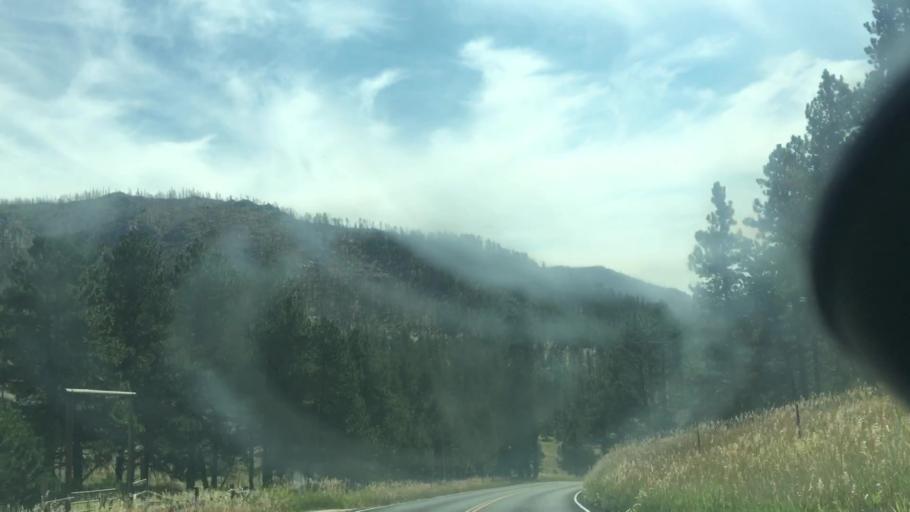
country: US
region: Colorado
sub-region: Larimer County
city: Laporte
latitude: 40.6031
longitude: -105.3428
